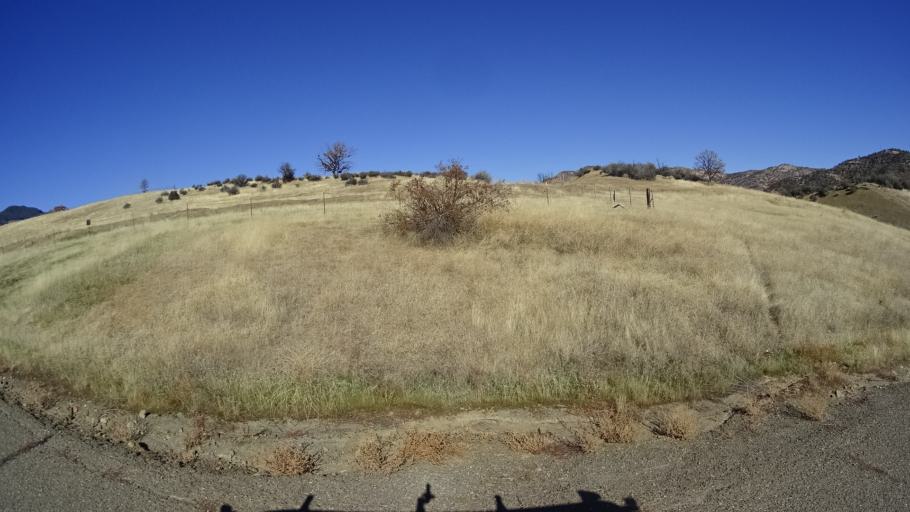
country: US
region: California
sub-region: Siskiyou County
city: Yreka
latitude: 41.9193
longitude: -122.5770
